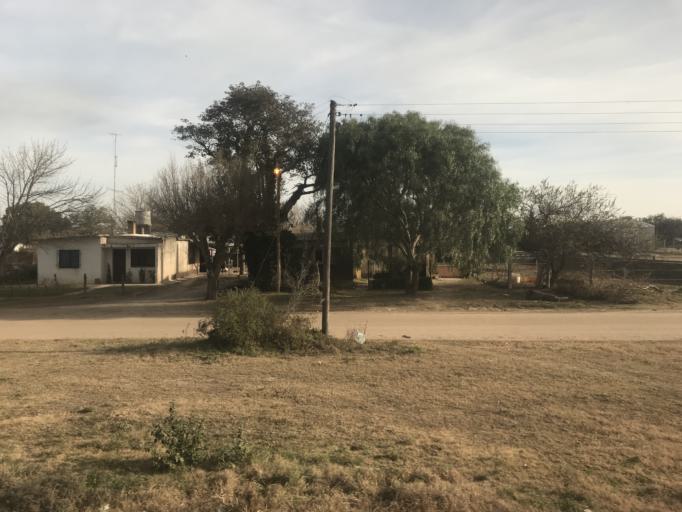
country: AR
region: Cordoba
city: Pilar
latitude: -31.6750
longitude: -63.8919
